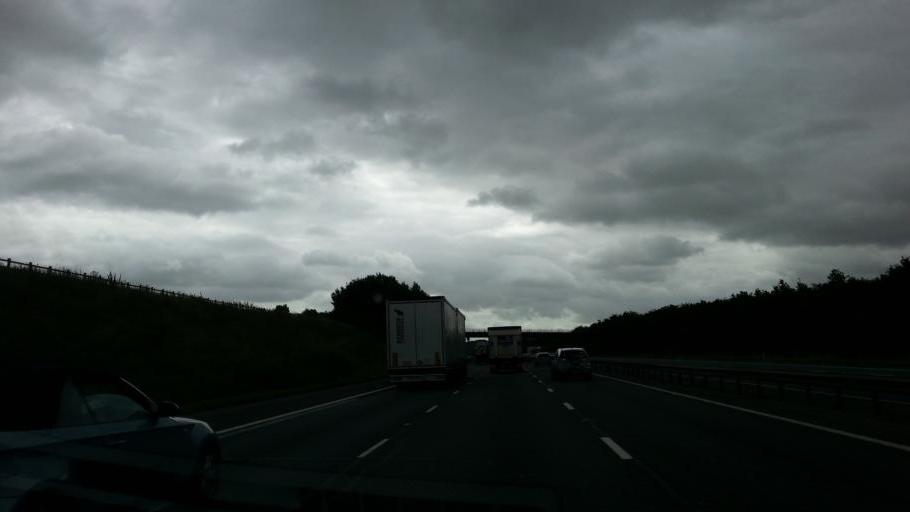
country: GB
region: England
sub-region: Warwickshire
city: Harbury
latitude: 52.2243
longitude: -1.5156
